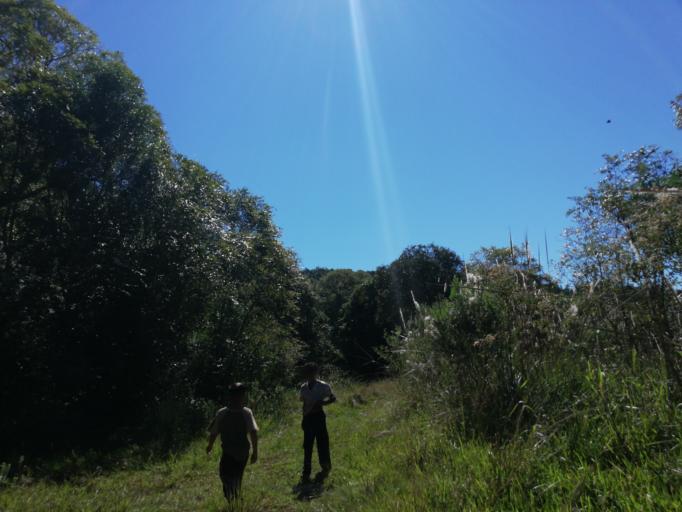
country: AR
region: Misiones
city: El Soberbio
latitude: -27.0605
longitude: -54.3753
